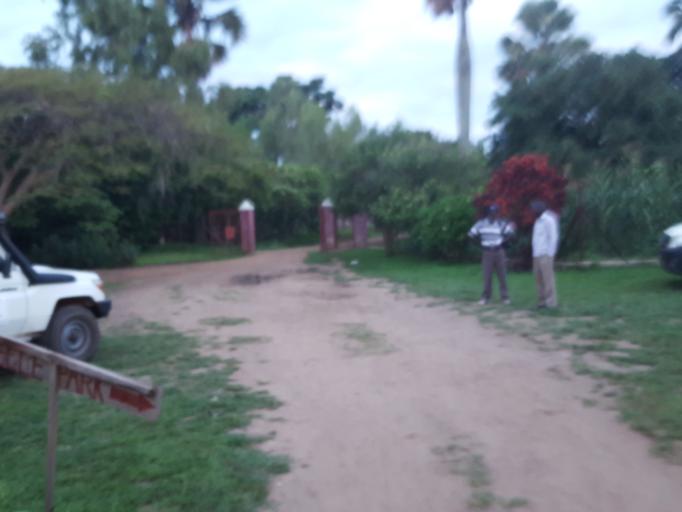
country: UG
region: Northern Region
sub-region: Yumbe District
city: Yumbe
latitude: 3.4168
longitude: 31.1163
